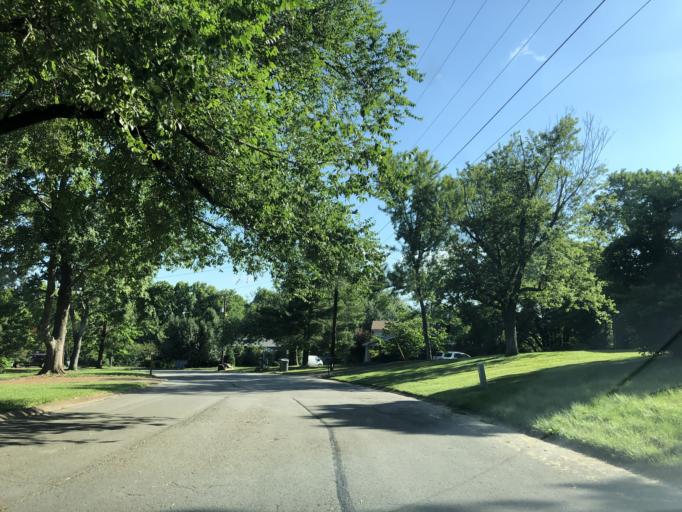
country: US
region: Tennessee
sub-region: Davidson County
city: Belle Meade
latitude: 36.0569
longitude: -86.9351
